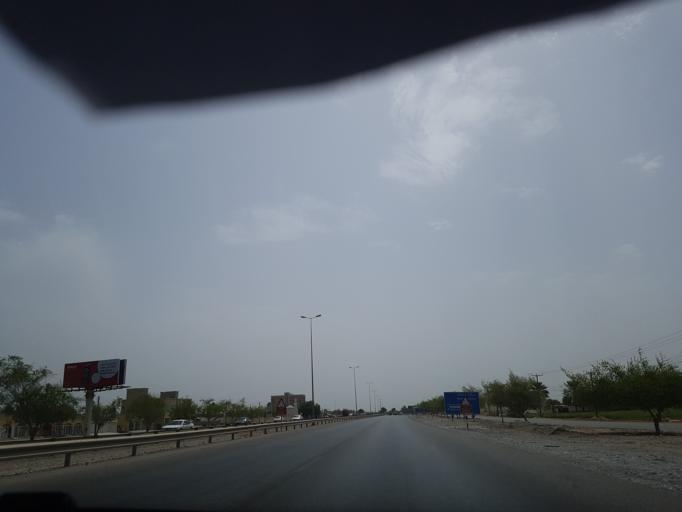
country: OM
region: Al Batinah
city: As Suwayq
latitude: 23.7410
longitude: 57.6381
